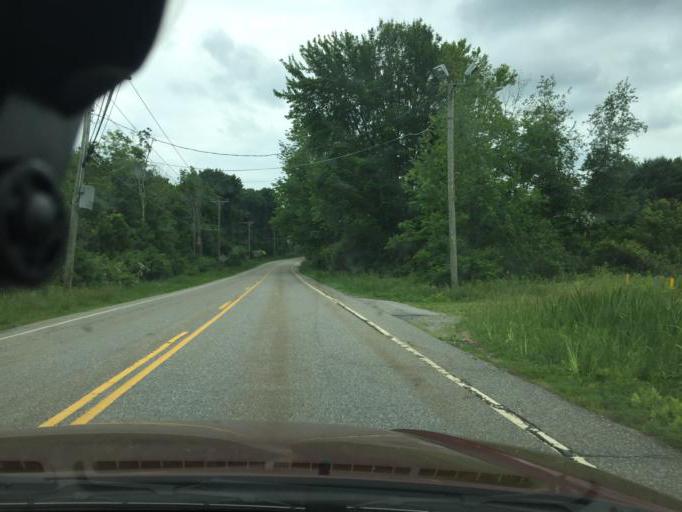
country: US
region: Connecticut
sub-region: Litchfield County
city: Litchfield
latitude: 41.7145
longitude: -73.2359
